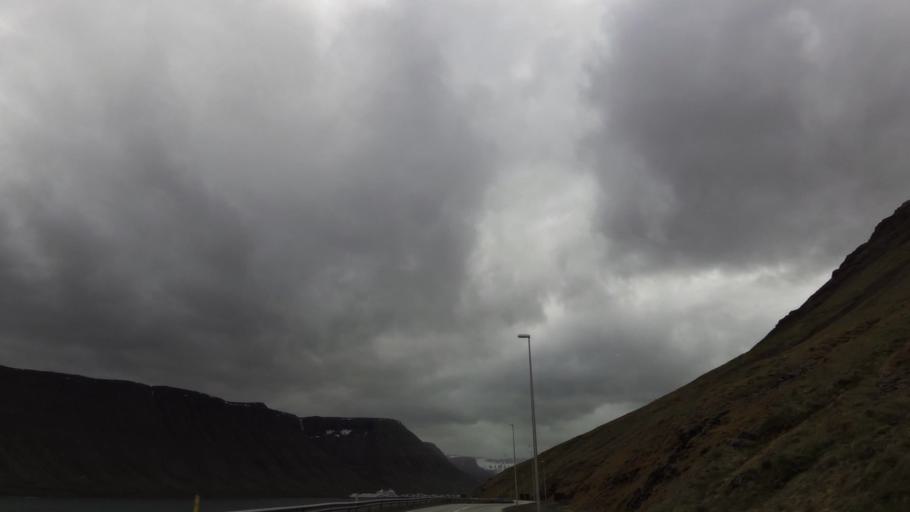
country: IS
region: Westfjords
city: Isafjoerdur
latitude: 66.0963
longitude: -23.1116
